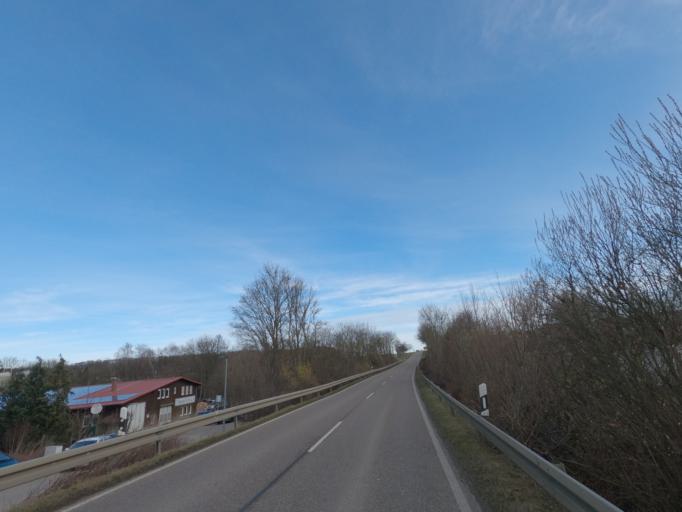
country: DE
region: Baden-Wuerttemberg
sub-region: Regierungsbezirk Stuttgart
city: Zell unter Aichelberg
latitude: 48.6493
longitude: 9.5652
